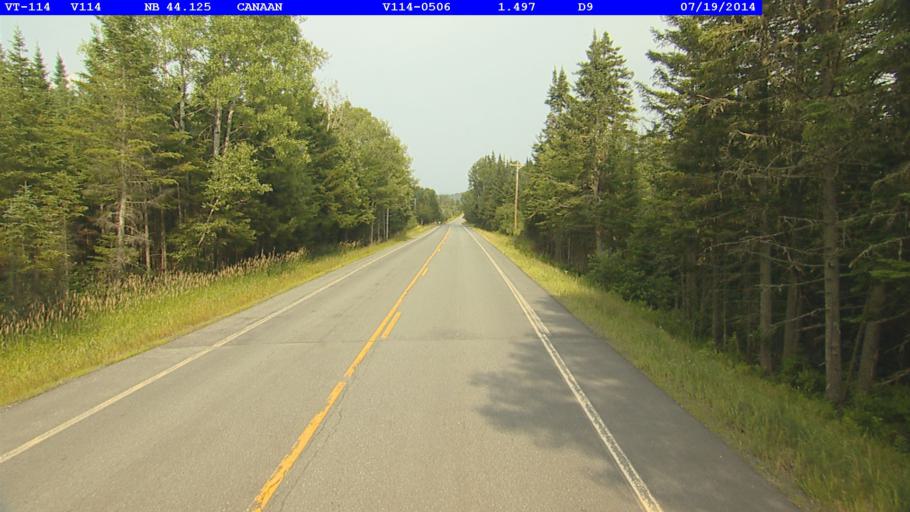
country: CA
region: Quebec
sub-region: Estrie
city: Coaticook
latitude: 45.0057
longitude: -71.6635
